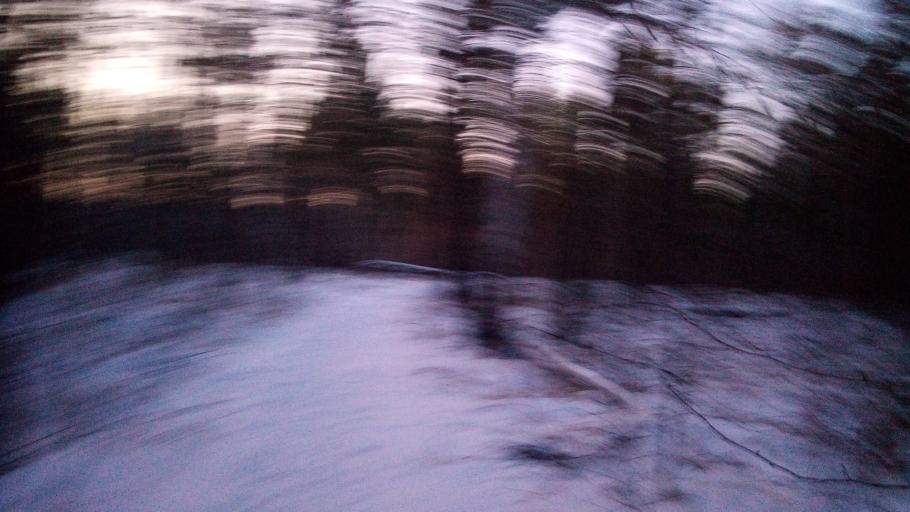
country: RU
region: Chelyabinsk
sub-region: Gorod Chelyabinsk
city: Chelyabinsk
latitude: 55.1636
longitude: 61.3322
